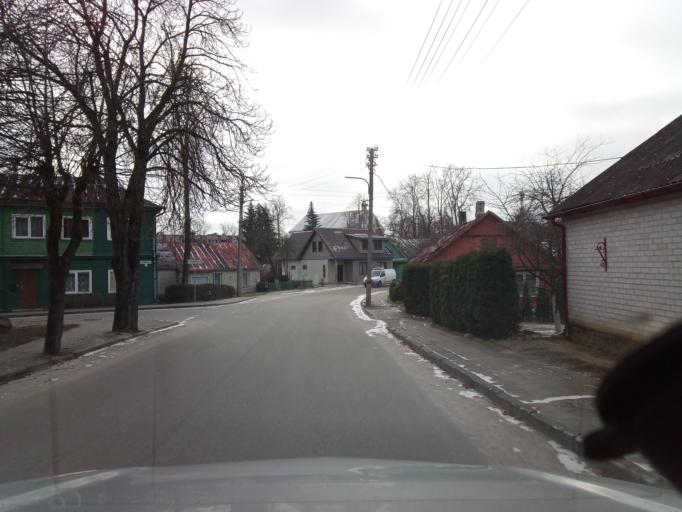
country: LT
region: Alytaus apskritis
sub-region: Alytaus rajonas
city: Daugai
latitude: 54.3617
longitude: 24.3436
